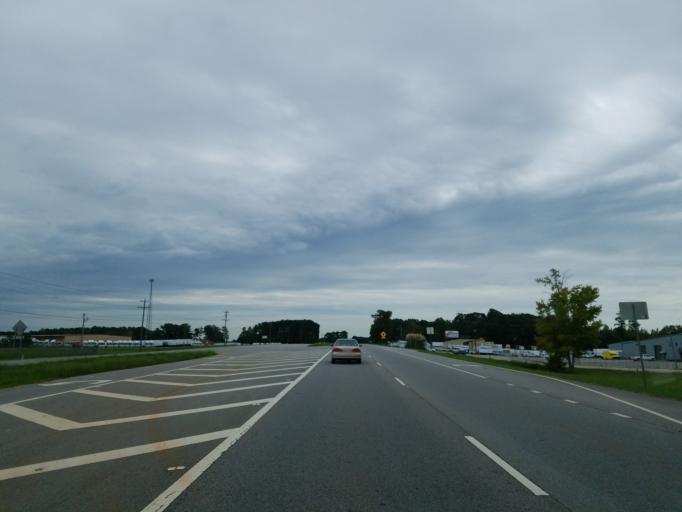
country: US
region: Georgia
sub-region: Spalding County
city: Griffin
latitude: 33.1755
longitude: -84.2661
